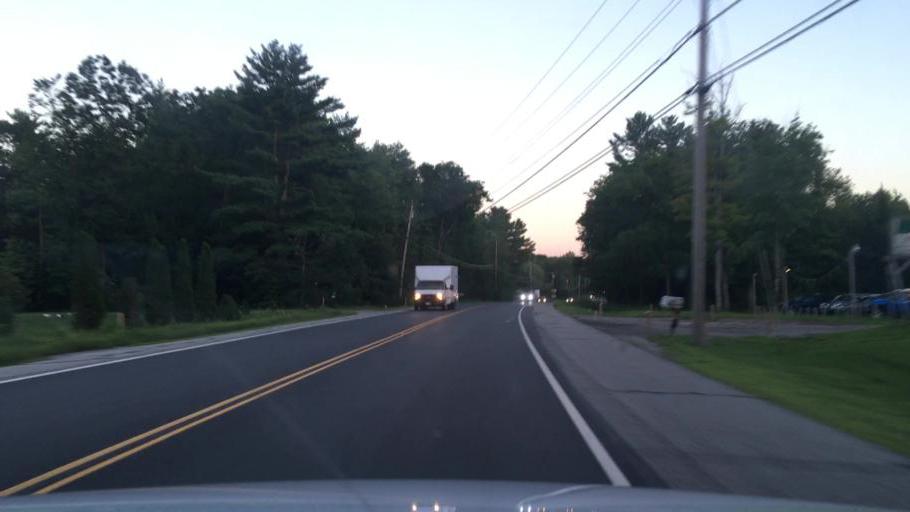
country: US
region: Maine
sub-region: Androscoggin County
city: Turner
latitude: 44.2244
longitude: -70.2498
